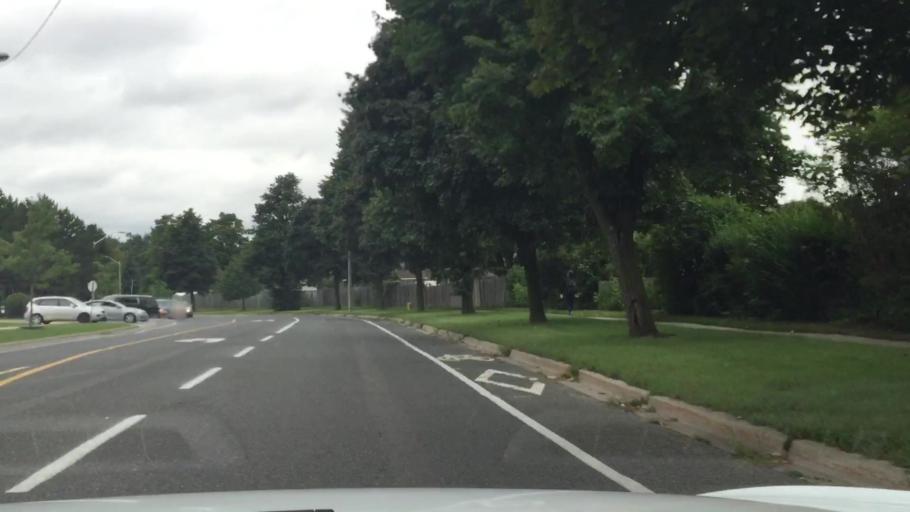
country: CA
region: Ontario
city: Scarborough
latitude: 43.7985
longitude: -79.2711
